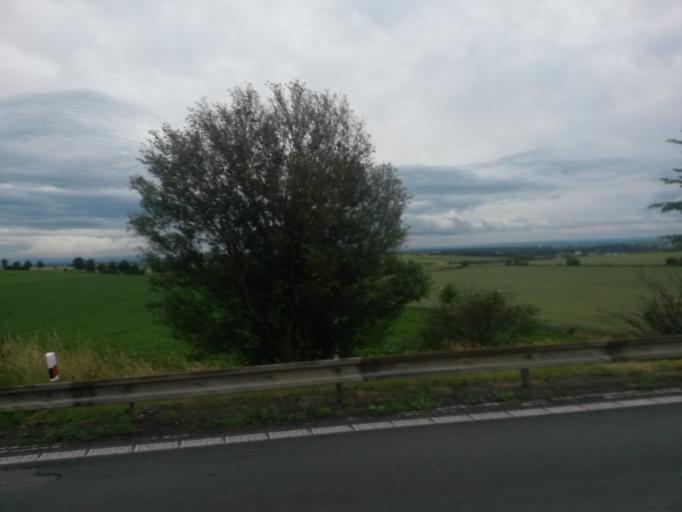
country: CZ
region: Olomoucky
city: Hnevotin
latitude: 49.5559
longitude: 17.1890
